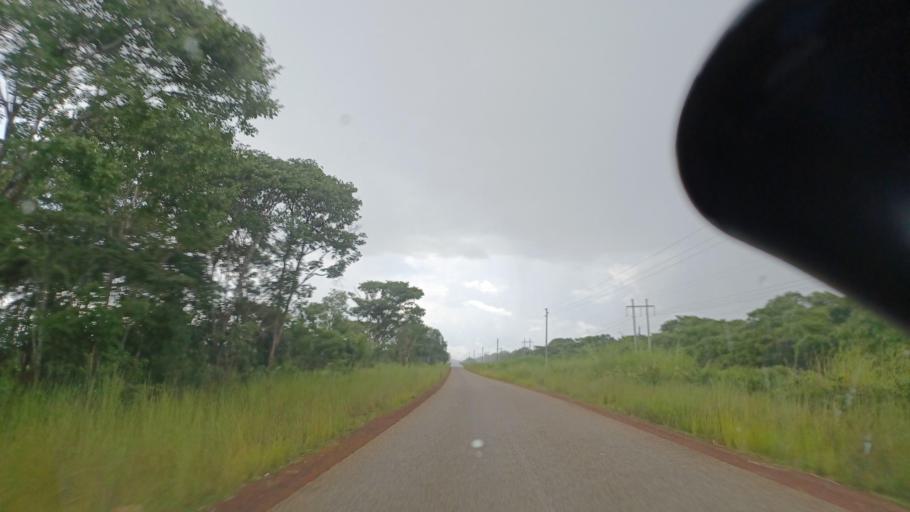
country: ZM
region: North-Western
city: Kasempa
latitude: -13.0923
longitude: 25.9243
